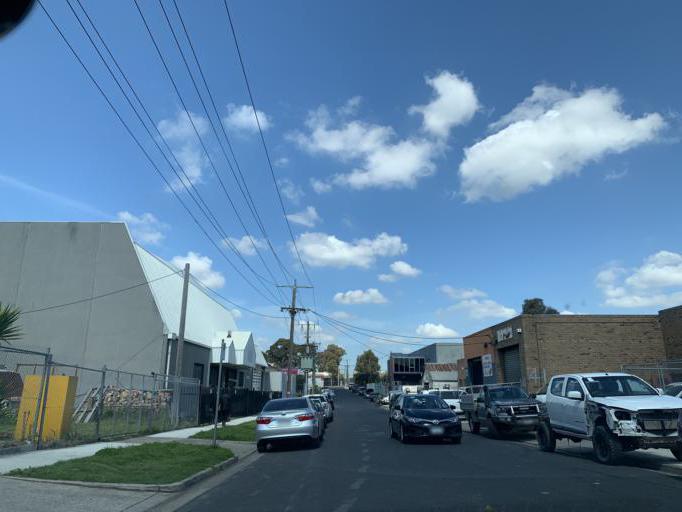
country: AU
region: Victoria
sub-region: Moreland
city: Coburg North
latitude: -37.7276
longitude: 144.9591
